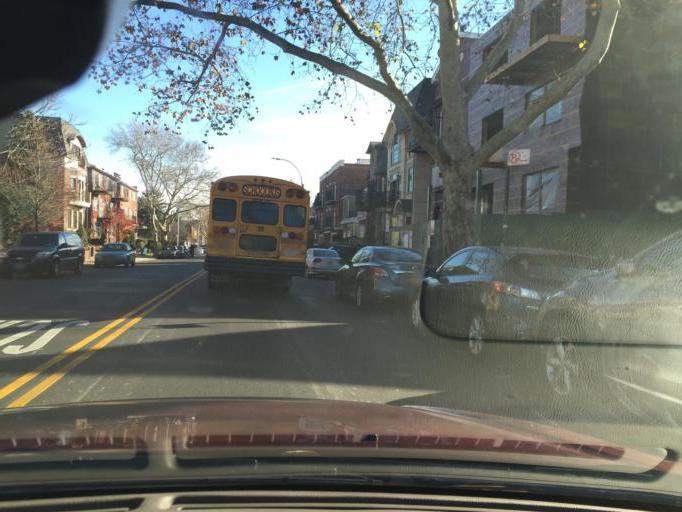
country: US
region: New York
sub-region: Kings County
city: Bensonhurst
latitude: 40.6247
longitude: -73.9917
